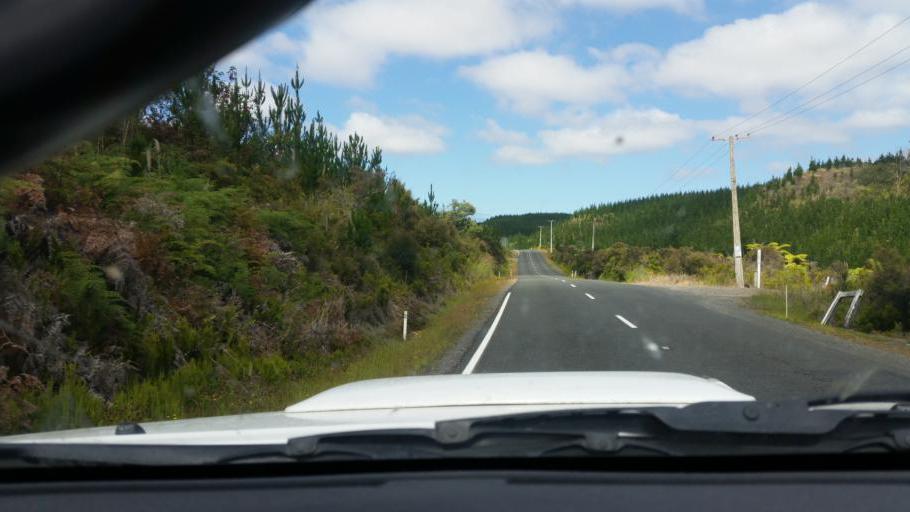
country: NZ
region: Northland
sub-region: Kaipara District
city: Dargaville
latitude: -35.8168
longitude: 173.7150
